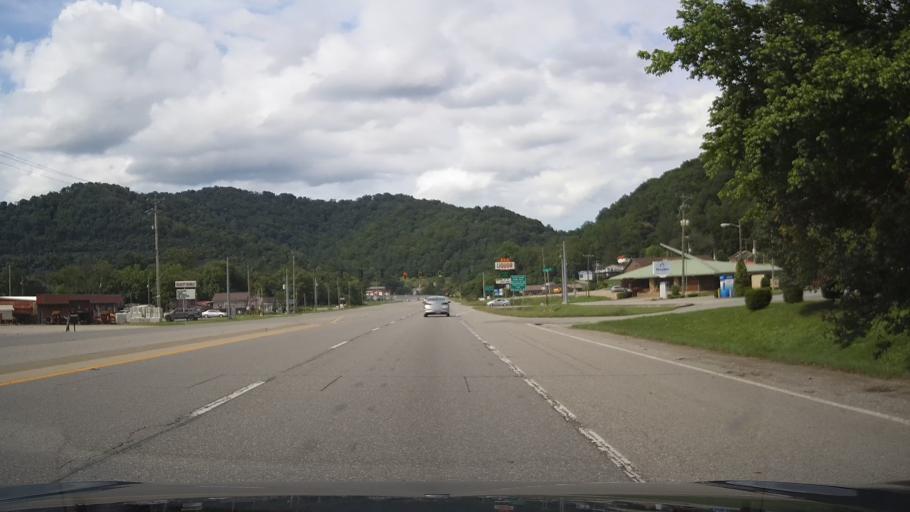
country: US
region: Kentucky
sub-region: Pike County
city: Coal Run Village
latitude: 37.5488
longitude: -82.6332
